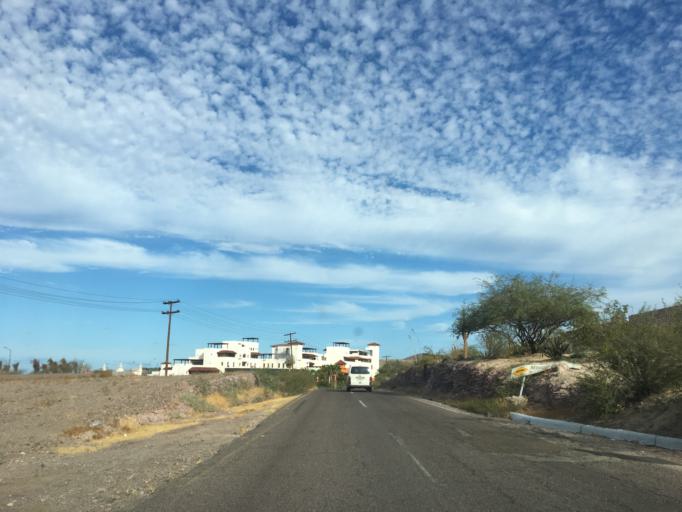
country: MX
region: Baja California Sur
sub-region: La Paz
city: La Paz
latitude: 24.2043
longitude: -110.2982
